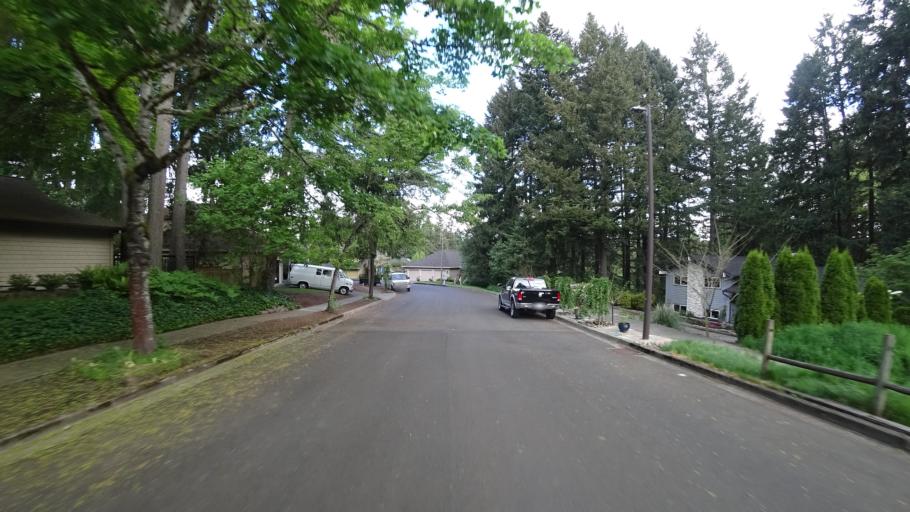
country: US
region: Oregon
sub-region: Washington County
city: Beaverton
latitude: 45.4691
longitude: -122.8281
